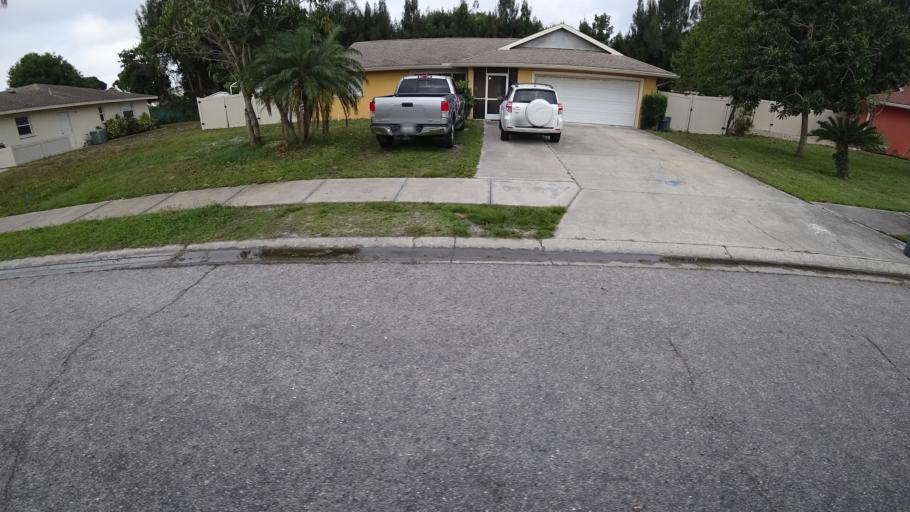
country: US
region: Florida
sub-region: Manatee County
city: Bayshore Gardens
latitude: 27.4327
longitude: -82.5918
